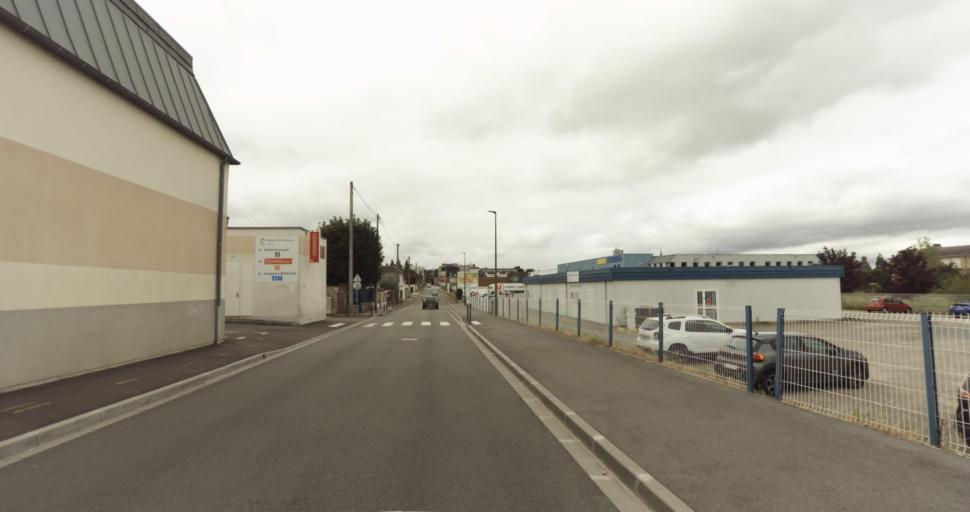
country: FR
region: Haute-Normandie
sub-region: Departement de l'Eure
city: Evreux
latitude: 49.0284
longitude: 1.1602
